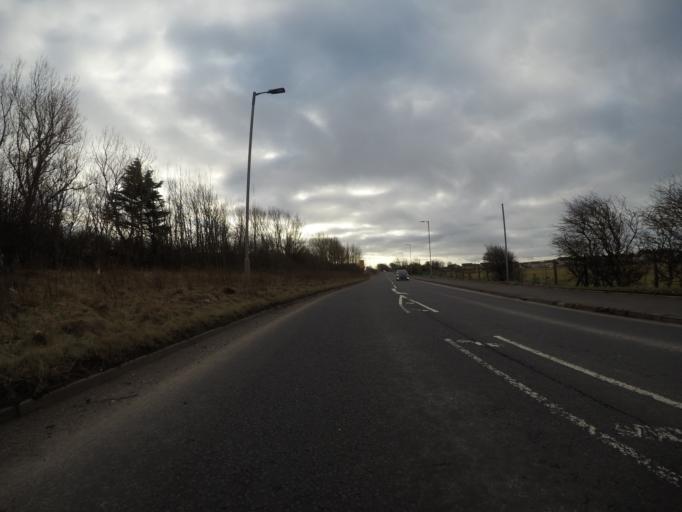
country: GB
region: Scotland
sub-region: North Ayrshire
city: Dreghorn
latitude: 55.5753
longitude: -4.6417
